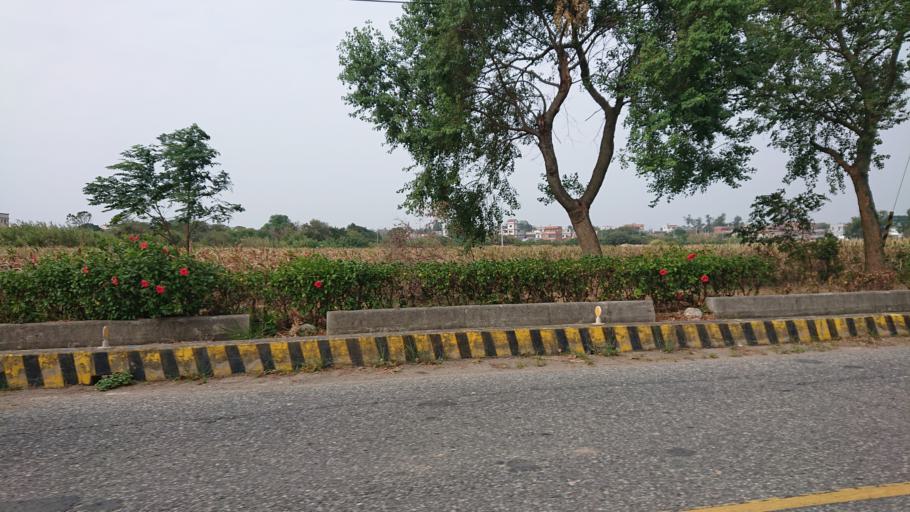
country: TW
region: Fukien
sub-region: Kinmen
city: Jincheng
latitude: 24.4699
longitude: 118.4001
